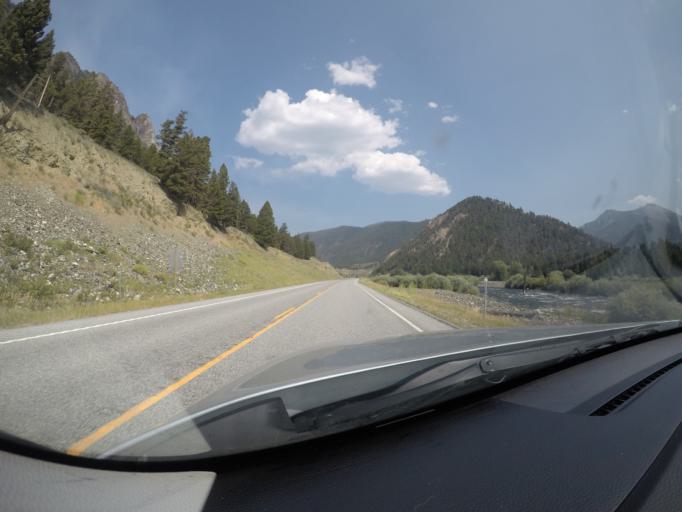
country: US
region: Montana
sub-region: Gallatin County
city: West Yellowstone
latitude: 44.8265
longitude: -111.4473
